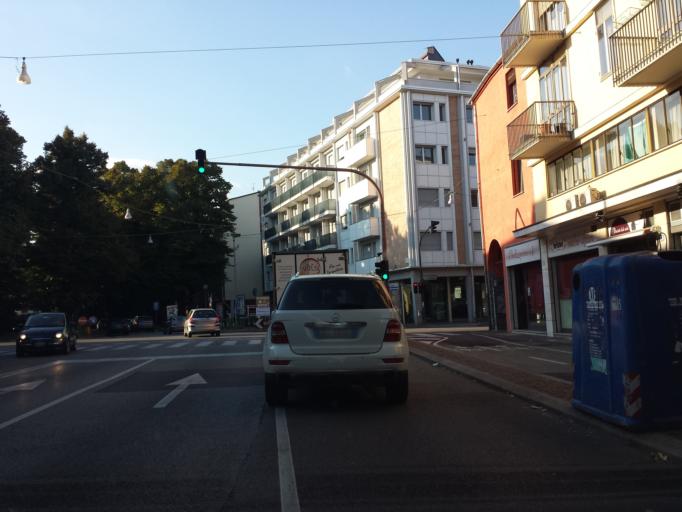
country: IT
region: Veneto
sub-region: Provincia di Padova
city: Padova
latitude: 45.4072
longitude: 11.8857
